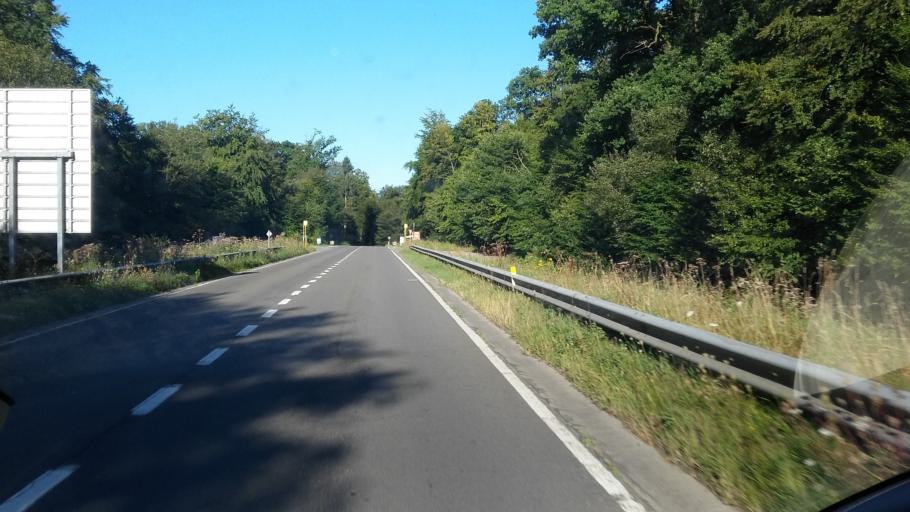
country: BE
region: Wallonia
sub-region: Province du Luxembourg
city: Leglise
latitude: 49.8087
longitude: 5.5132
